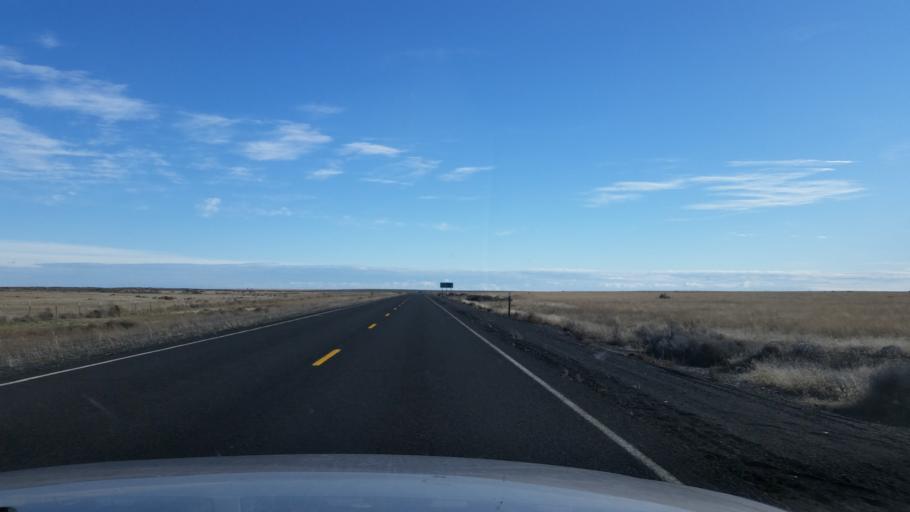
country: US
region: Washington
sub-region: Grant County
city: Moses Lake North
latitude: 47.3642
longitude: -118.9745
